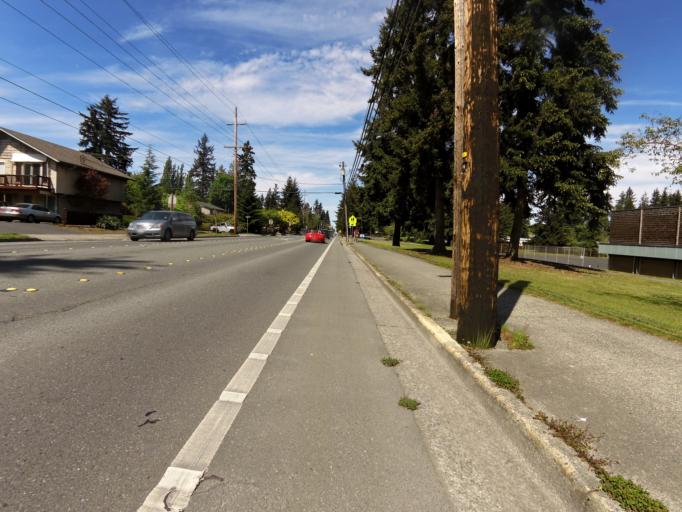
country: US
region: Washington
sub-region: Snohomish County
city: Lynnwood
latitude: 47.8119
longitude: -122.3357
